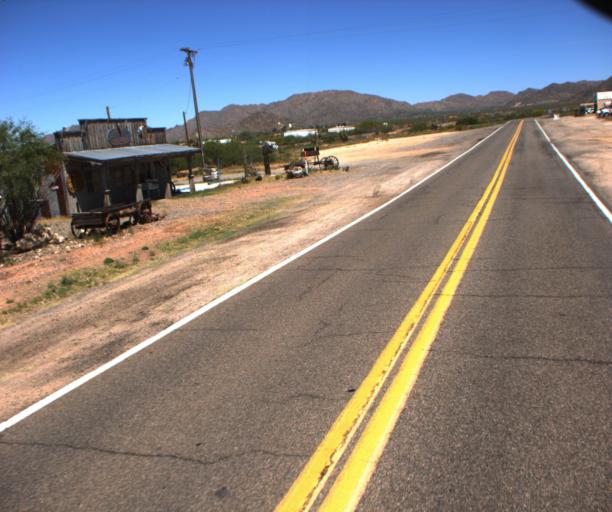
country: US
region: Arizona
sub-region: Yavapai County
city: Congress
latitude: 34.1585
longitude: -112.8444
